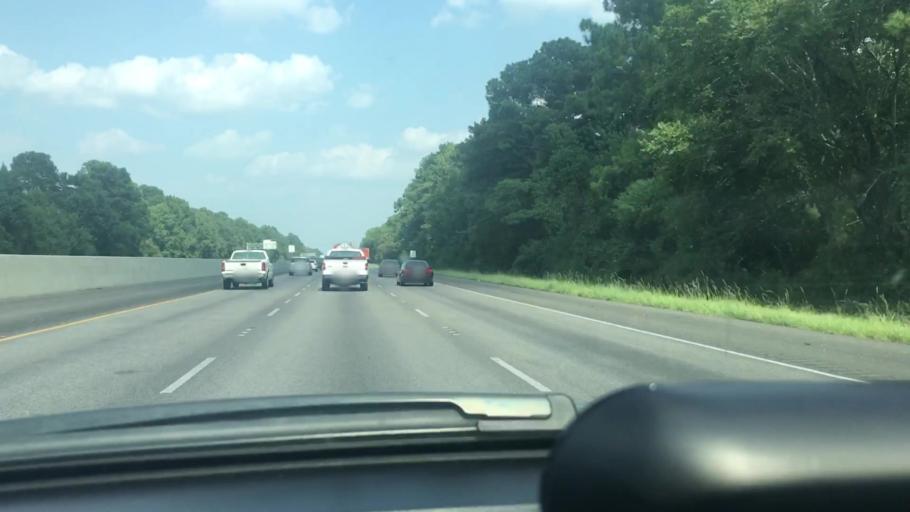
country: US
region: Louisiana
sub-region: Livingston Parish
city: Walker
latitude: 30.4654
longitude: -90.9079
